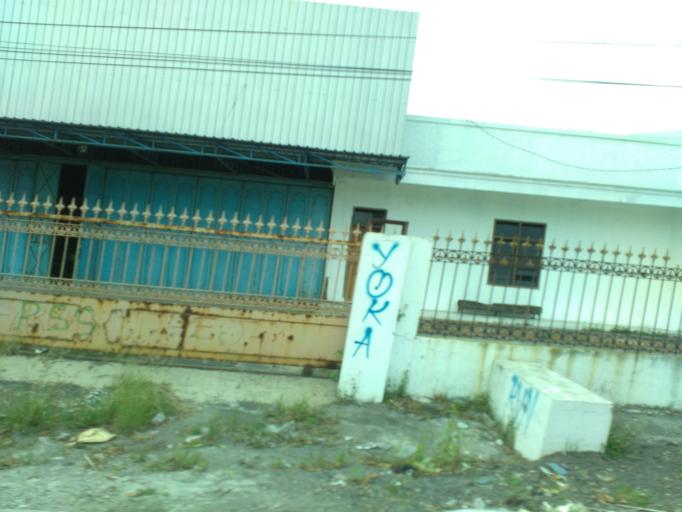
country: ID
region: Central Java
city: Trucuk
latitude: -7.6857
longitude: 110.6412
